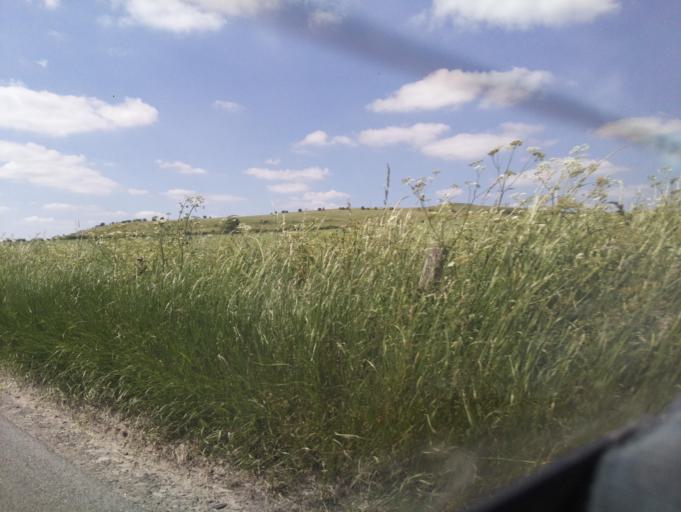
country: GB
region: England
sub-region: Wiltshire
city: Woodborough
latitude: 51.3637
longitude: -1.8758
